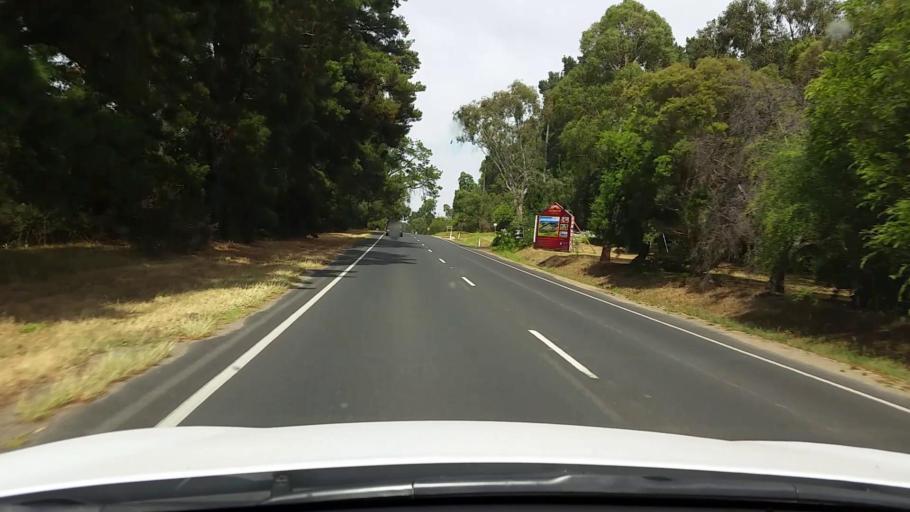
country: AU
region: Victoria
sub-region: Mornington Peninsula
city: Balnarring
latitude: -38.3665
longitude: 145.1372
